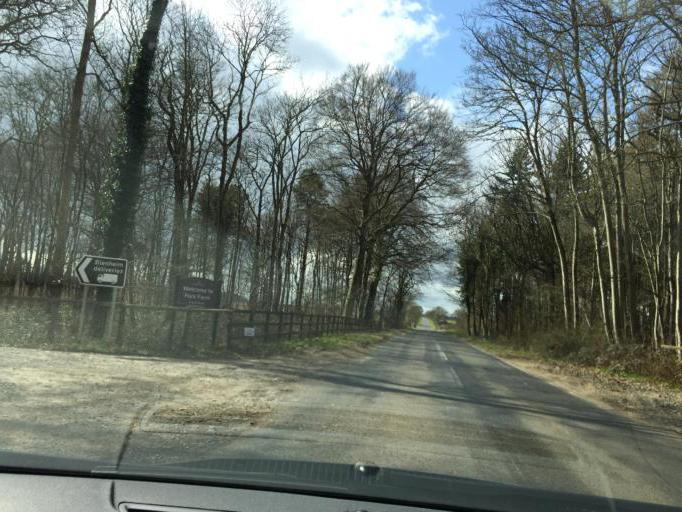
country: GB
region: England
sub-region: Oxfordshire
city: Stonesfield
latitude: 51.8629
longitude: -1.3991
